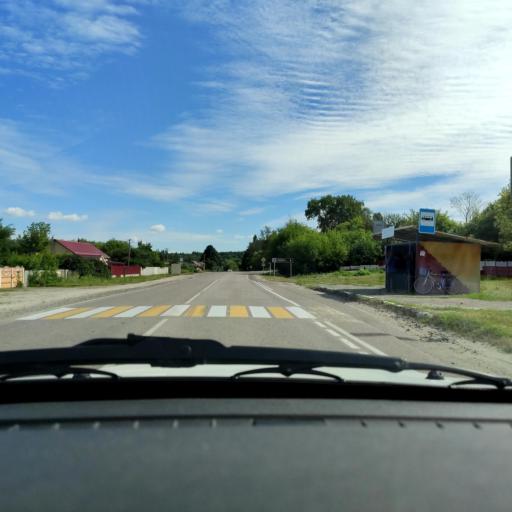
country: RU
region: Voronezj
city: Uglyanets
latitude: 51.8543
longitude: 39.6650
